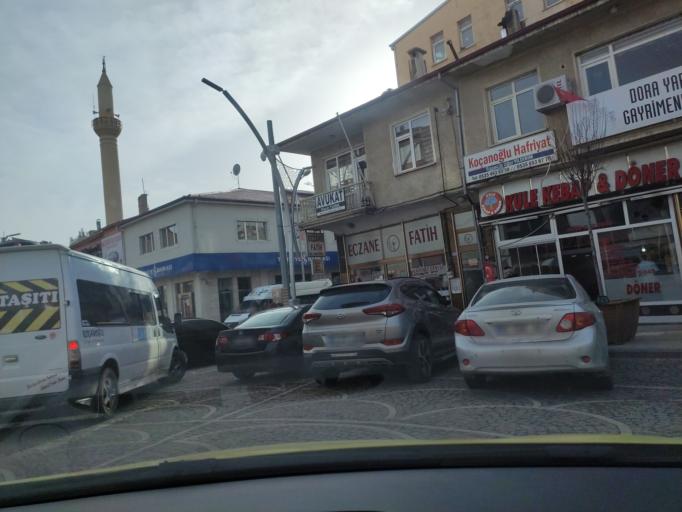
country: TR
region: Bayburt
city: Bayburt
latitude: 40.2604
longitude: 40.2272
